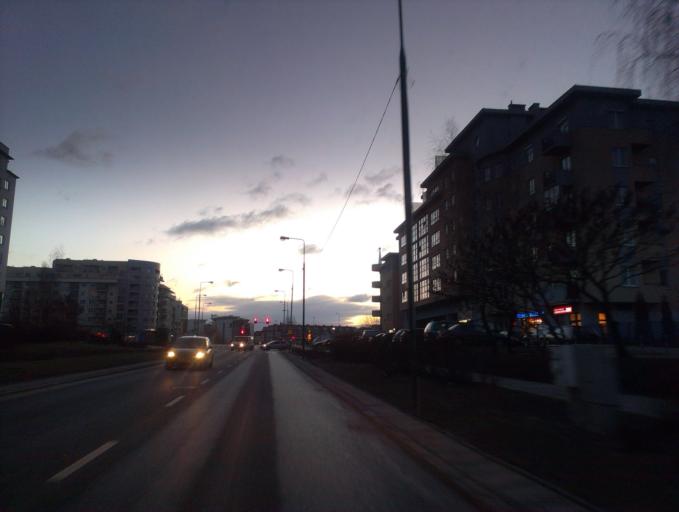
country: PL
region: Masovian Voivodeship
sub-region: Warszawa
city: Kabaty
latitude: 52.1312
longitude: 21.0635
